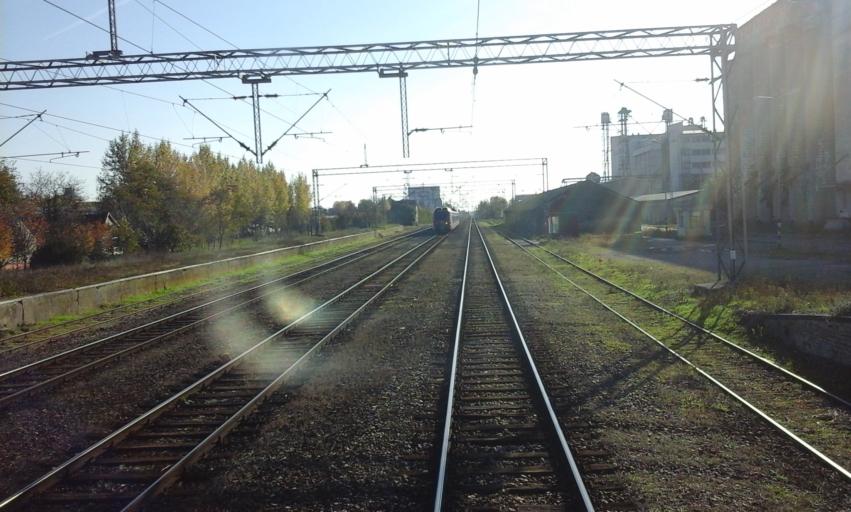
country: RS
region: Autonomna Pokrajina Vojvodina
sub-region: Severnobacki Okrug
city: Backa Topola
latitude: 45.8170
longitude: 19.6495
